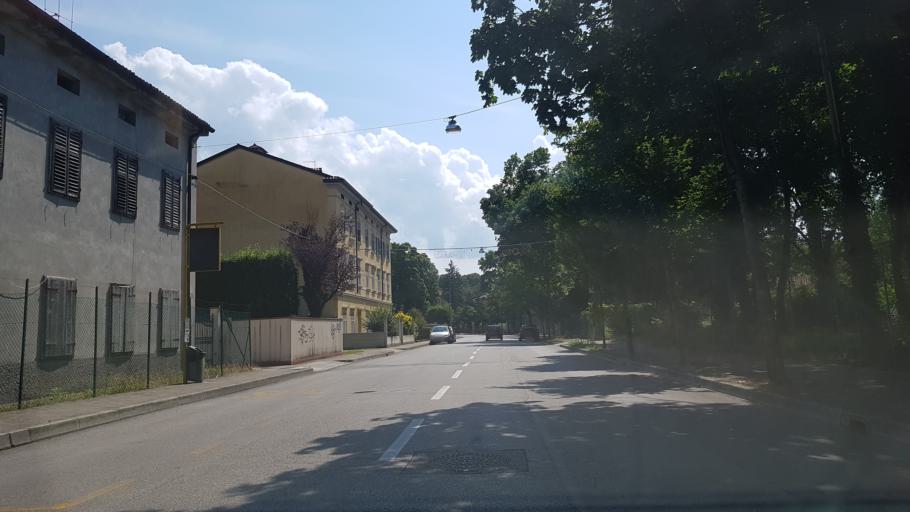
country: SI
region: Nova Gorica
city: Nova Gorica
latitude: 45.9558
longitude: 13.6310
